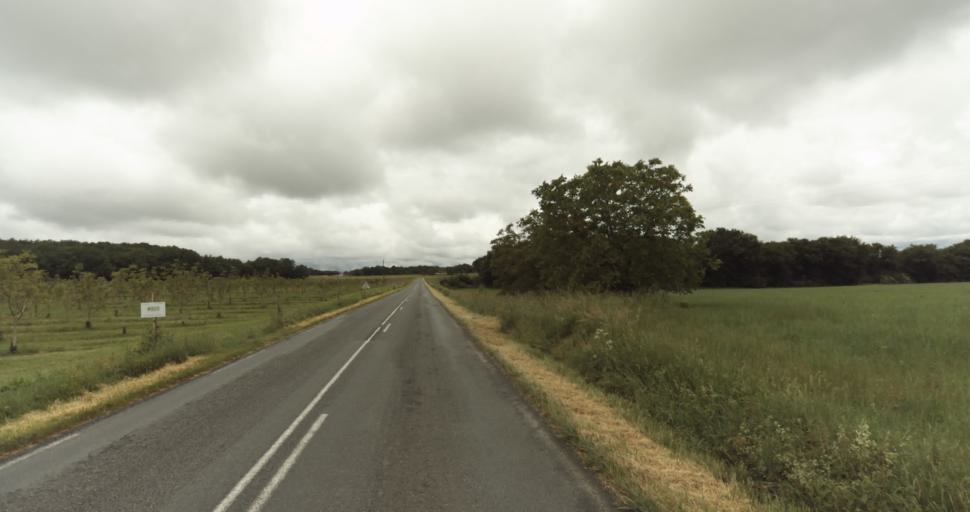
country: FR
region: Aquitaine
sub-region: Departement de la Dordogne
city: Beaumont-du-Perigord
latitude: 44.6963
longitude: 0.8606
